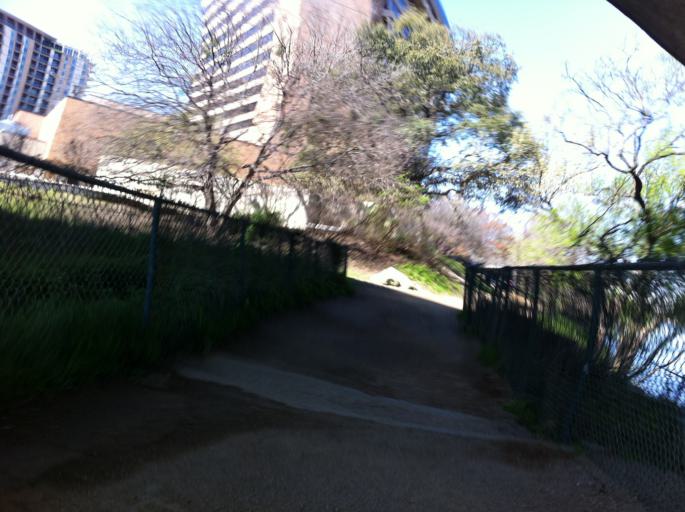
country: US
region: Texas
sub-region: Travis County
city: Austin
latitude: 30.2599
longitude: -97.7443
